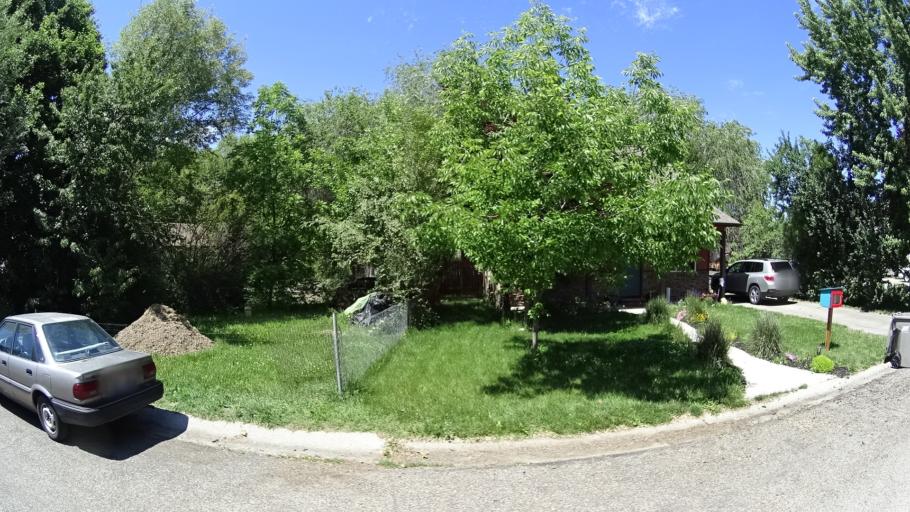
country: US
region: Idaho
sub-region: Ada County
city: Boise
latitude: 43.6021
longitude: -116.2236
